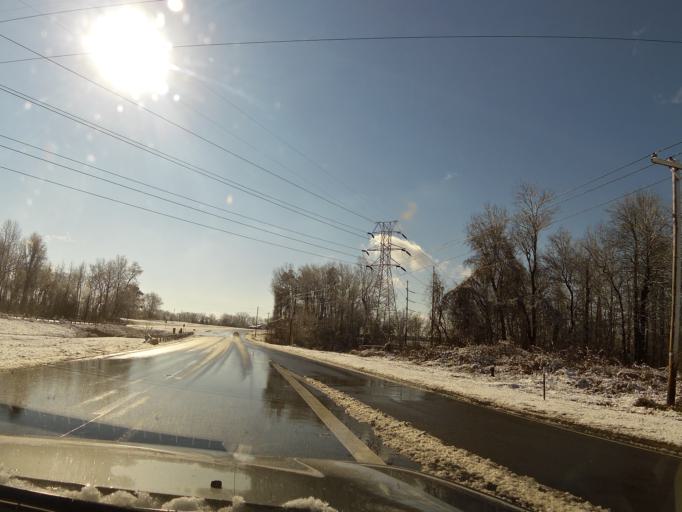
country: US
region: North Carolina
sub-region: Wilson County
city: Elm City
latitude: 35.7819
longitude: -77.8587
